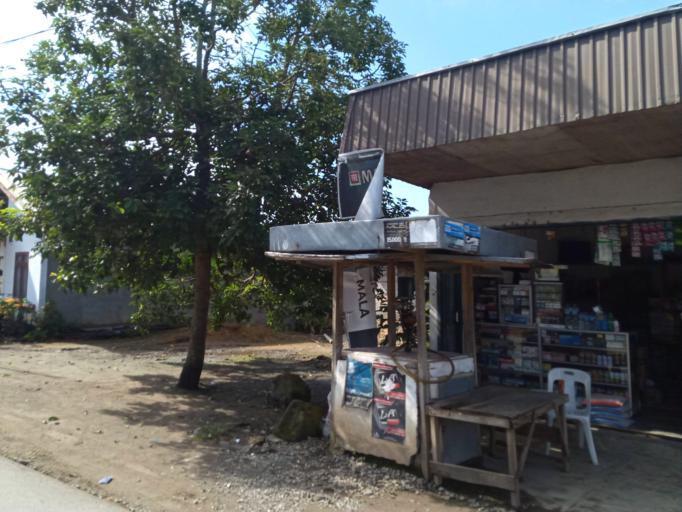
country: ID
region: Jambi
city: Sungai Penuh
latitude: -2.1627
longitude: 101.5872
